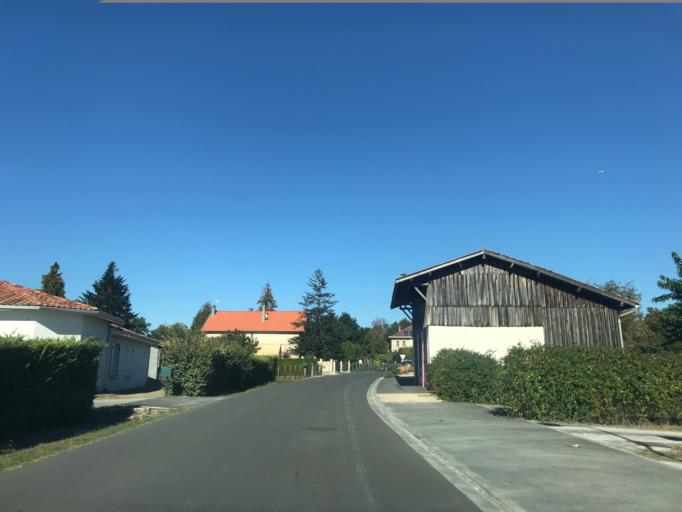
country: FR
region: Aquitaine
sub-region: Departement de la Gironde
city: Marcheprime
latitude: 44.6544
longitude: -0.8522
